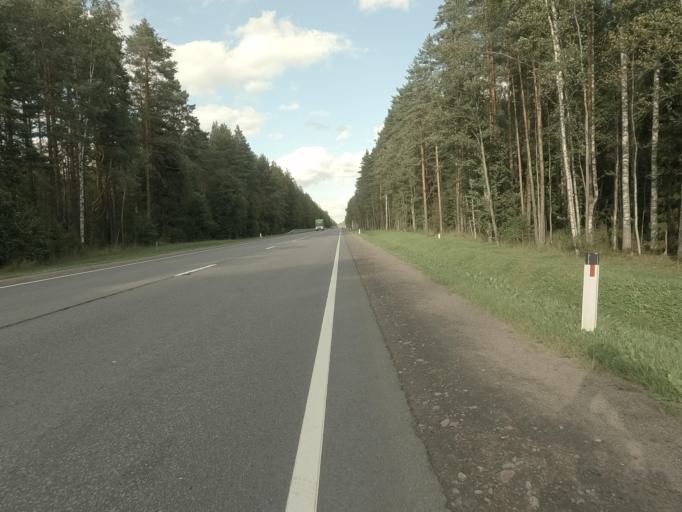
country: RU
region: Leningrad
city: Mga
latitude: 59.7018
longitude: 31.0020
